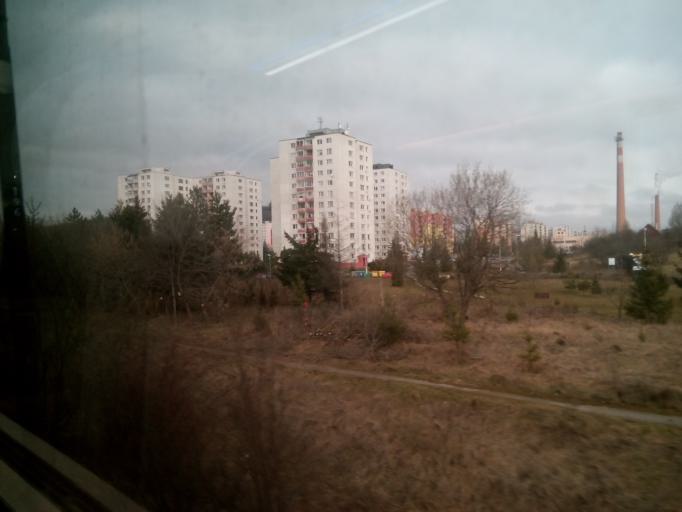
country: SK
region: Zilinsky
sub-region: Okres Liptovsky Mikulas
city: Liptovsky Mikulas
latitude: 49.0758
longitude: 19.6549
